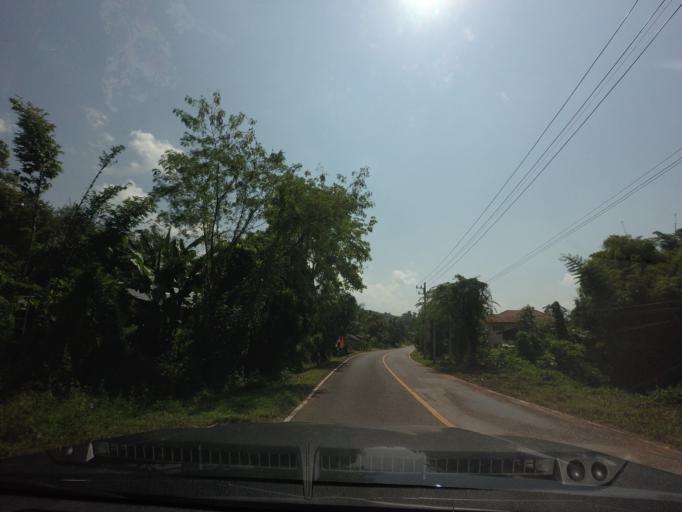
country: TH
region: Nan
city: Bo Kluea
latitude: 19.0776
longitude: 101.1578
